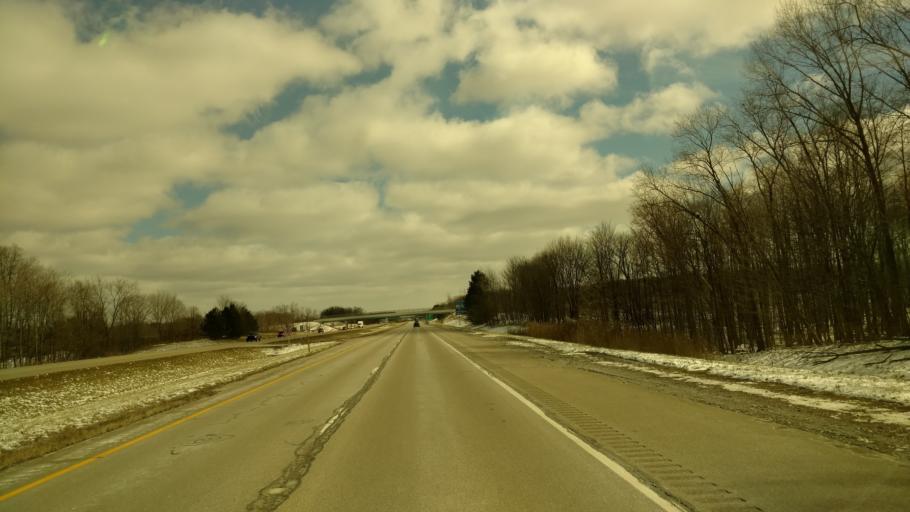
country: US
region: Ohio
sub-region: Ashtabula County
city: Geneva
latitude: 41.7687
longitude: -80.9640
